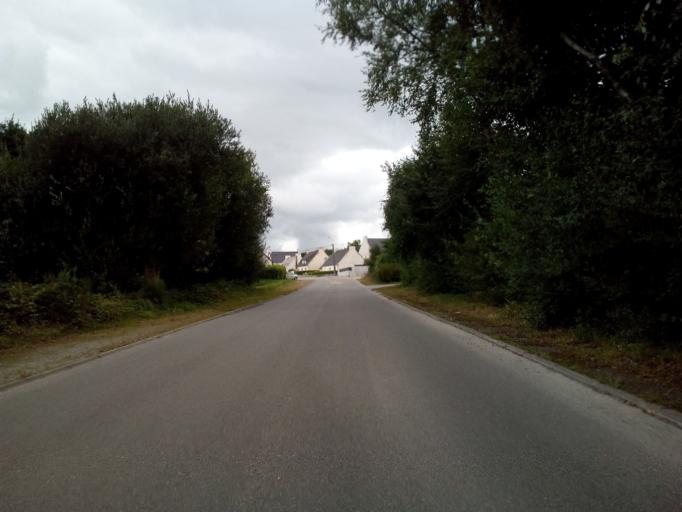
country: FR
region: Brittany
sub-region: Departement du Finistere
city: Landivisiau
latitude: 48.5131
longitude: -4.0558
